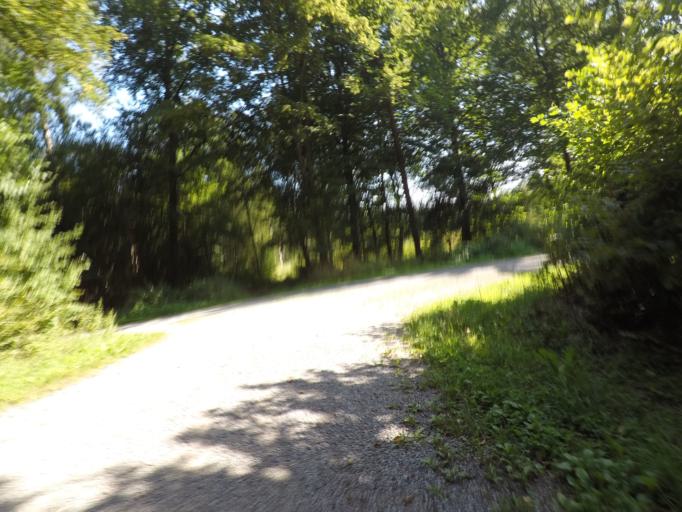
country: DE
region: Baden-Wuerttemberg
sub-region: Regierungsbezirk Stuttgart
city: Altdorf
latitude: 48.6617
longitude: 8.9804
